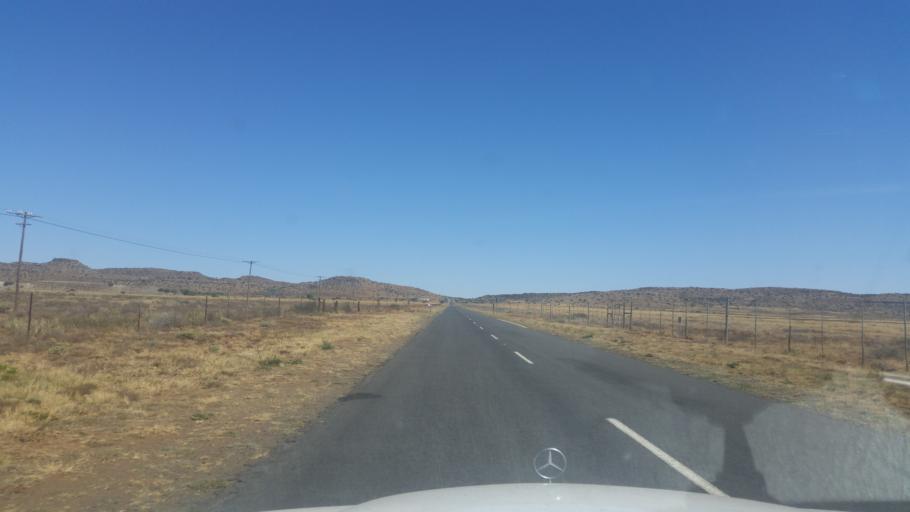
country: ZA
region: Eastern Cape
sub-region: Joe Gqabi District Municipality
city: Burgersdorp
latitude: -30.7830
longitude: 25.7743
